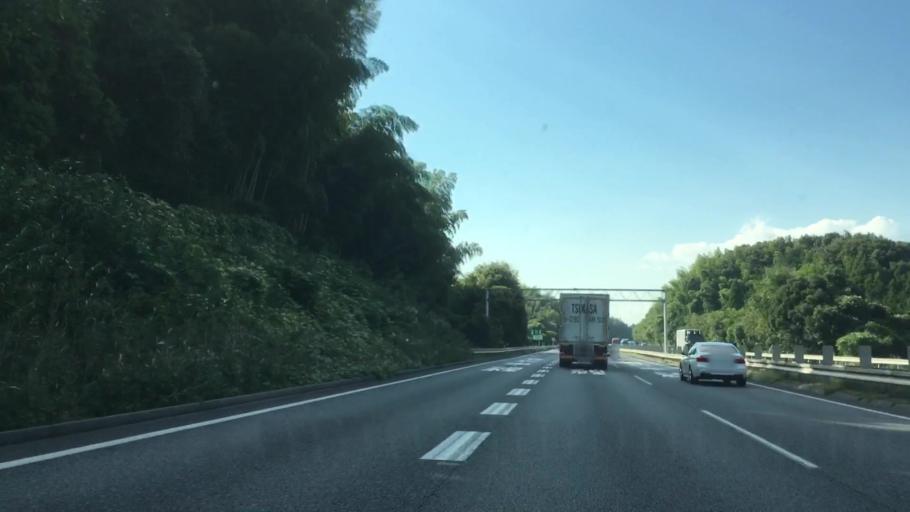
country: JP
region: Yamaguchi
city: Hikari
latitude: 34.0301
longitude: 131.9399
